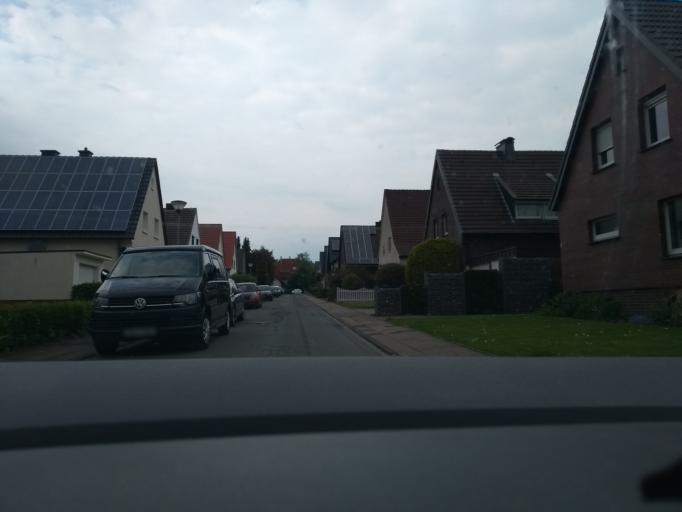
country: DE
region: North Rhine-Westphalia
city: Selm
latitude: 51.6626
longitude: 7.4640
